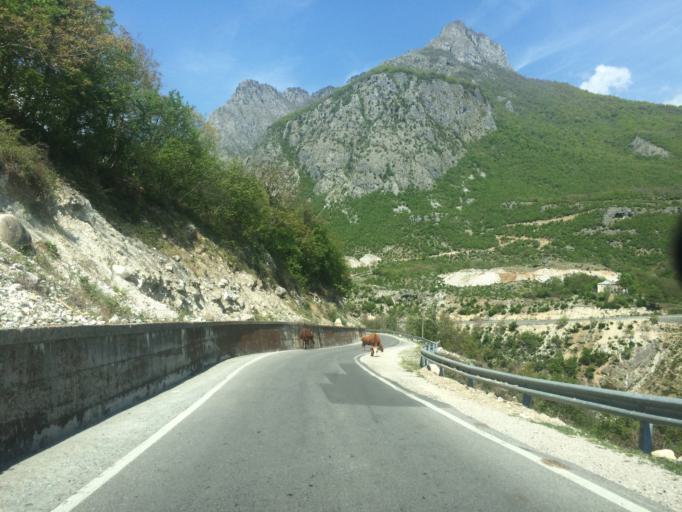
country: AL
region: Kukes
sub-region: Rrethi i Tropojes
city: Bajram Curri
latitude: 42.3860
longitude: 20.0768
